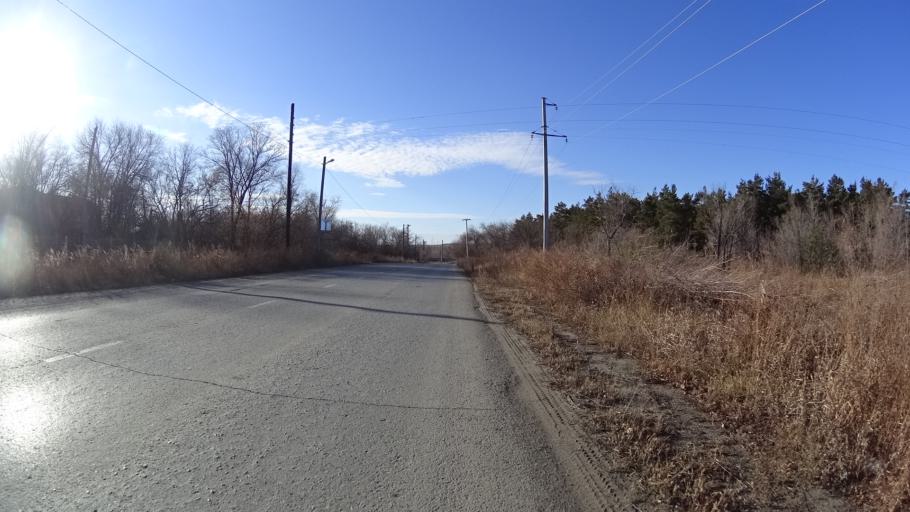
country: RU
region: Chelyabinsk
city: Troitsk
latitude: 54.0486
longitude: 61.6232
